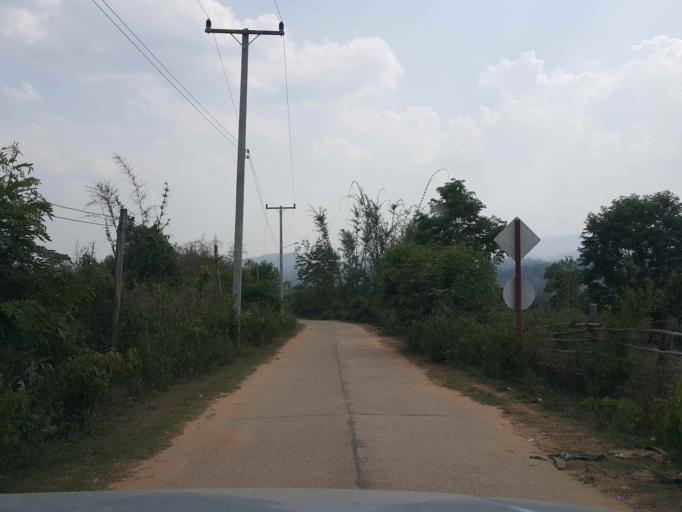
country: TH
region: Chiang Mai
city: Wiang Haeng
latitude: 19.4041
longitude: 98.7232
